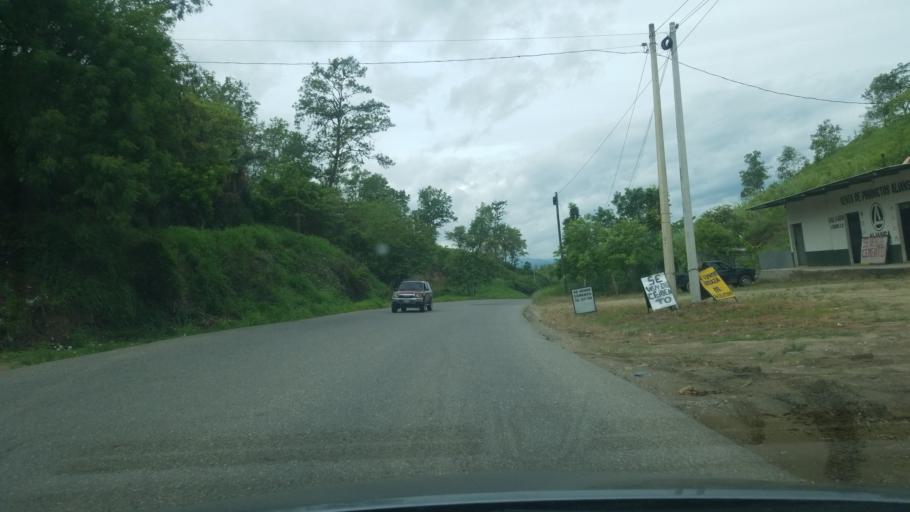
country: HN
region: Santa Barbara
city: La Flecha
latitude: 15.2978
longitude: -88.4573
